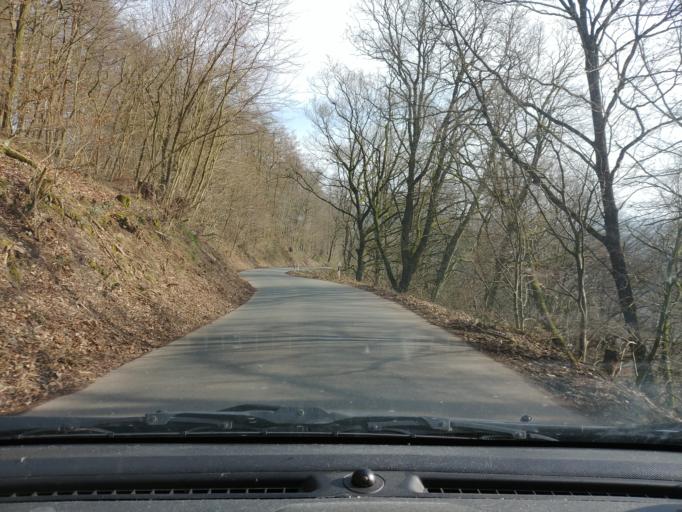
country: DE
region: Lower Saxony
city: Bad Karlshafen
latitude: 51.6499
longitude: 9.4428
